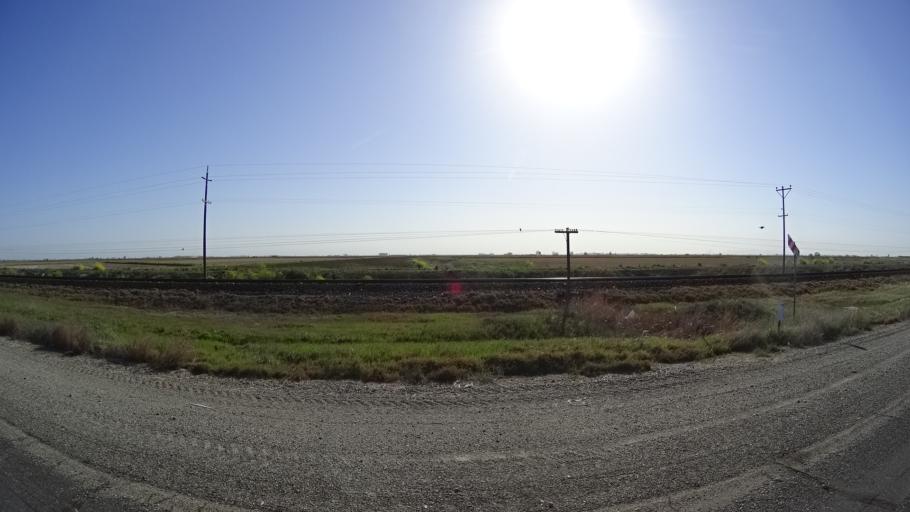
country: US
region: California
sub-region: Glenn County
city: Willows
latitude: 39.4698
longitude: -122.1930
